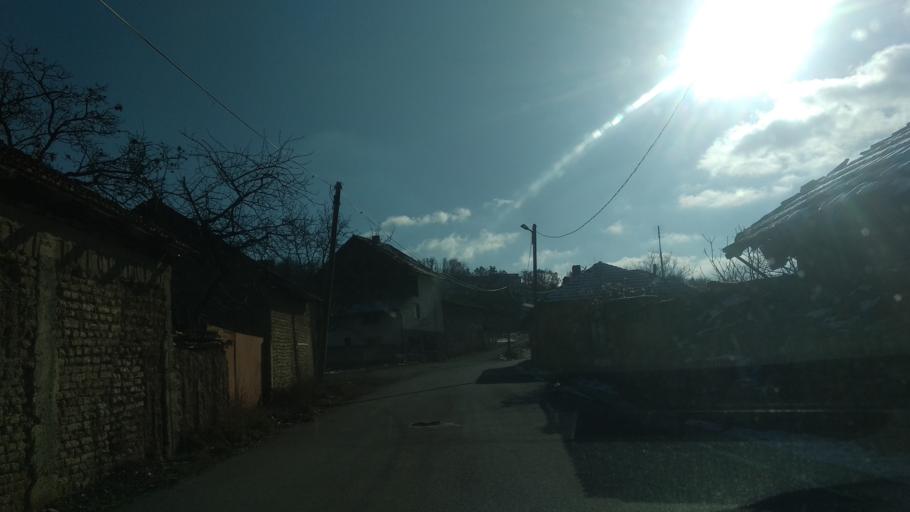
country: XK
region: Pristina
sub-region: Komuna e Prishtines
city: Pristina
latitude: 42.7148
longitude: 21.1691
